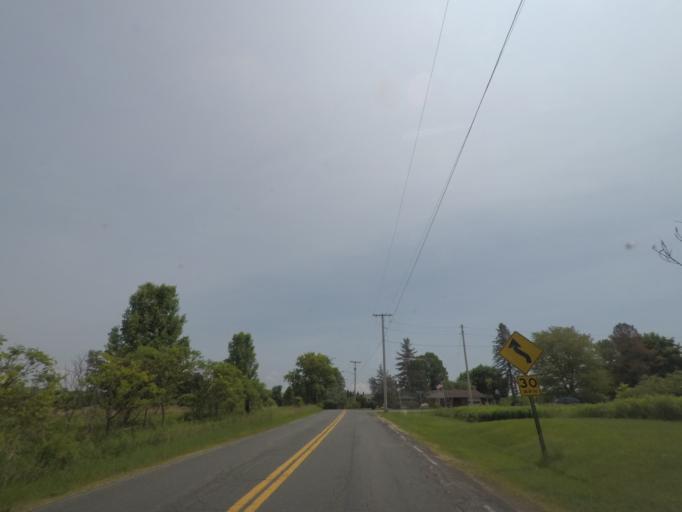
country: US
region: New York
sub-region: Rensselaer County
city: Castleton-on-Hudson
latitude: 42.4981
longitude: -73.7060
